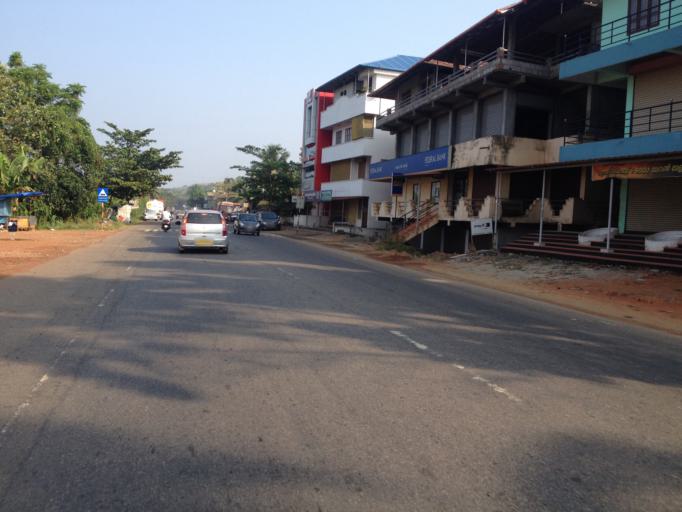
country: IN
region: Kerala
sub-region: Pattanamtitta
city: Adur
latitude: 9.0929
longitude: 76.7531
